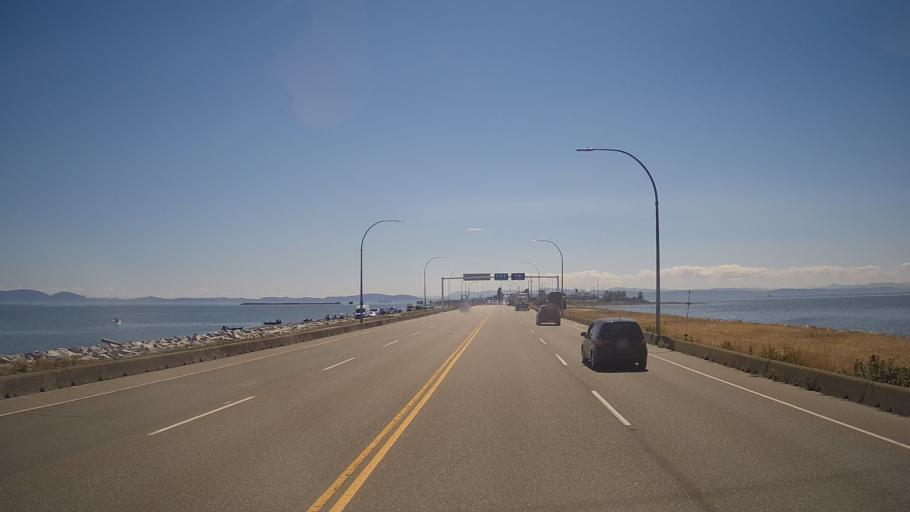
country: US
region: Washington
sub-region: Whatcom County
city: Point Roberts
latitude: 49.0180
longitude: -123.1145
